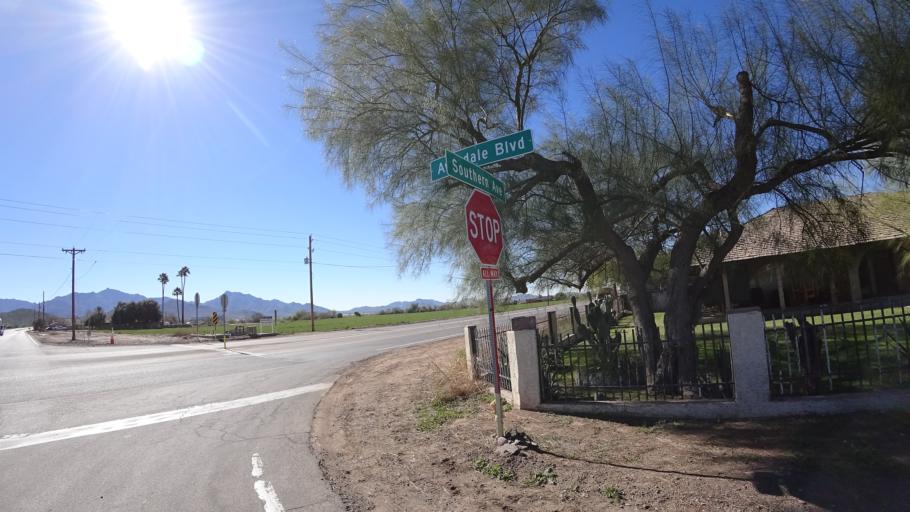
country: US
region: Arizona
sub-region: Maricopa County
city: Avondale
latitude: 33.3919
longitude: -112.3062
